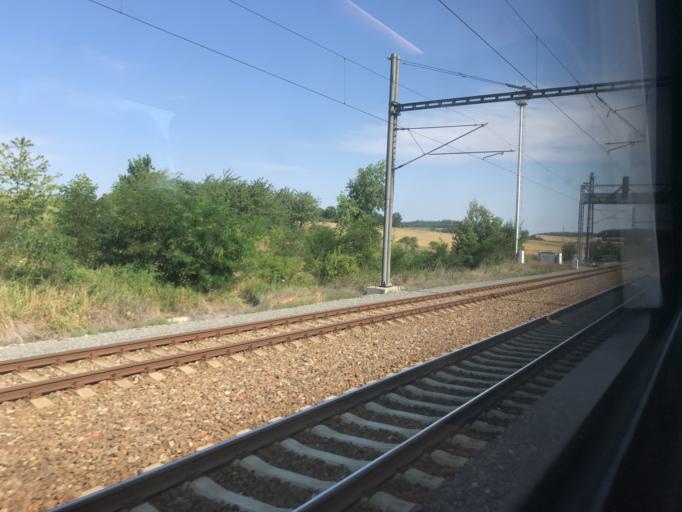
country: CZ
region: Central Bohemia
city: Votice
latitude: 49.6719
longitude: 14.6264
